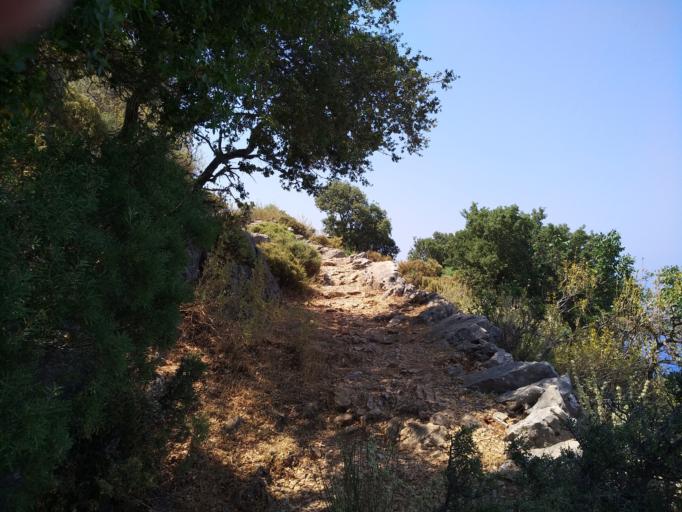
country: TR
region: Mugla
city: OEluedeniz
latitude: 36.5437
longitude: 29.1339
